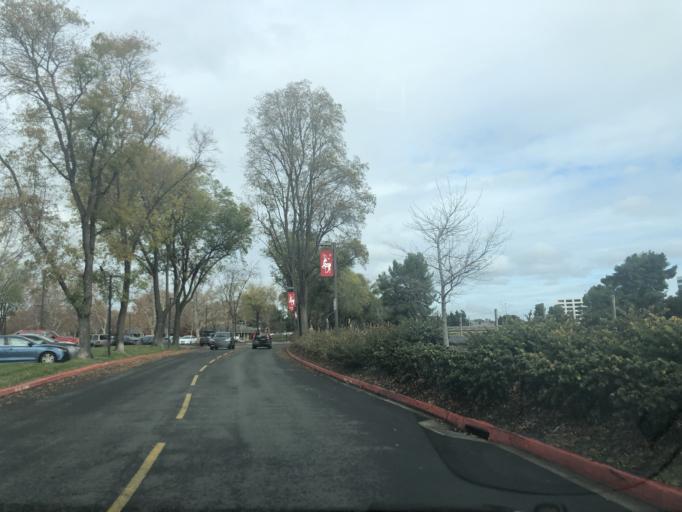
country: US
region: California
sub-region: Contra Costa County
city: Pleasant Hill
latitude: 37.9678
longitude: -122.0555
